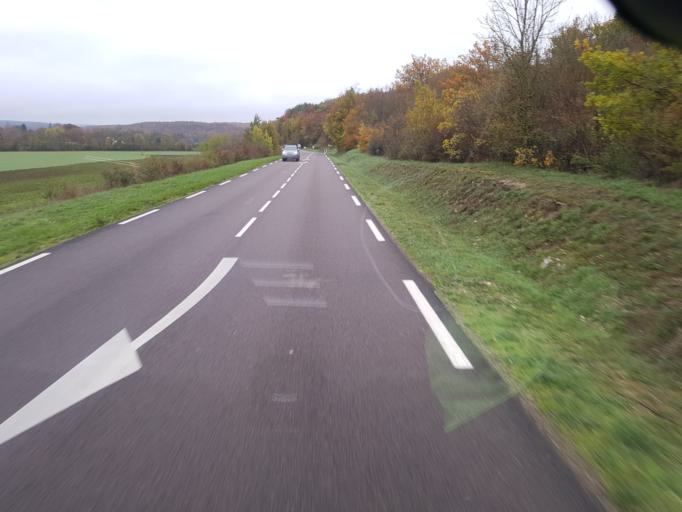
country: FR
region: Bourgogne
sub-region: Departement de la Cote-d'Or
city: Is-sur-Tille
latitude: 47.5296
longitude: 4.9940
